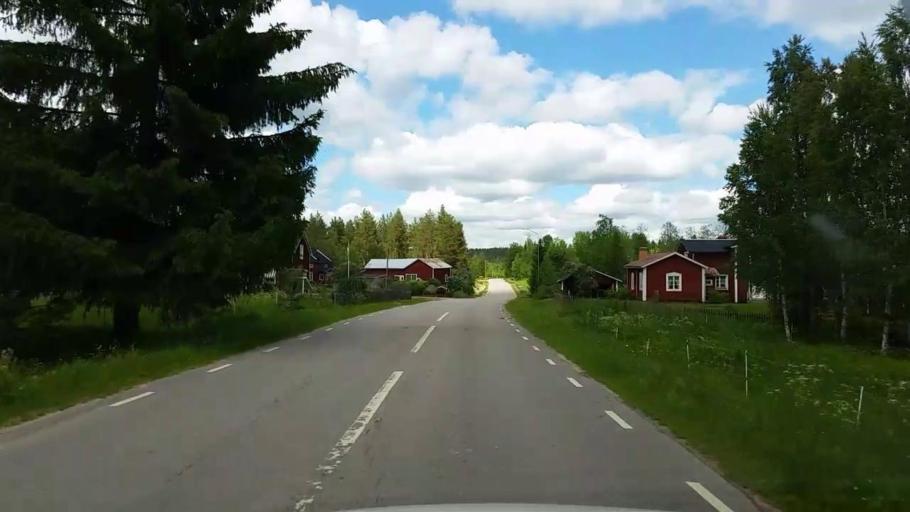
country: SE
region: Gaevleborg
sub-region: Ovanakers Kommun
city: Alfta
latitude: 61.3996
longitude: 16.0480
